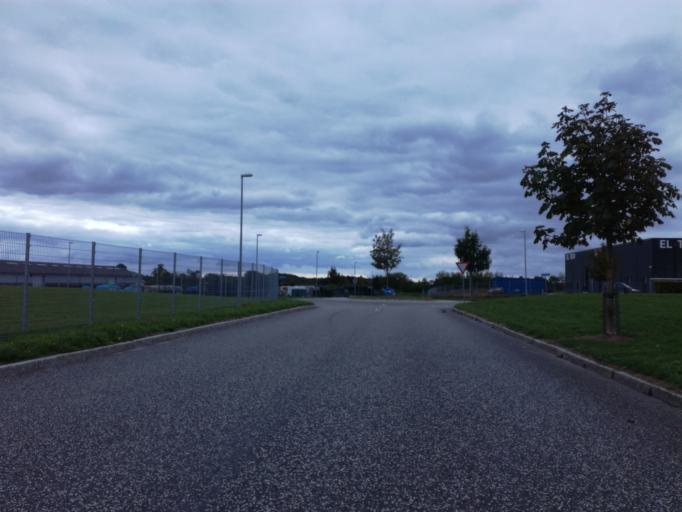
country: DK
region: South Denmark
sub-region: Vejle Kommune
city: Borkop
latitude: 55.6701
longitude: 9.5962
